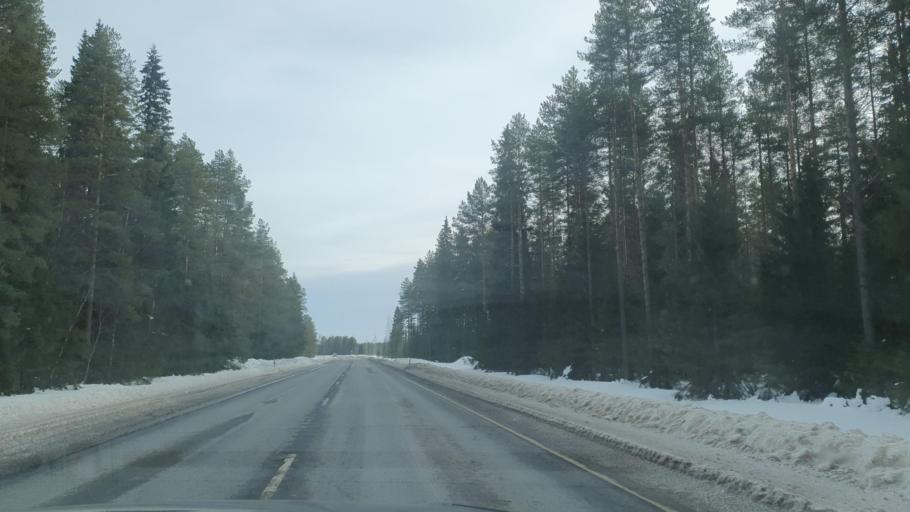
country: FI
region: Kainuu
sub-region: Kajaani
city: Vaala
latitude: 64.6160
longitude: 26.6098
